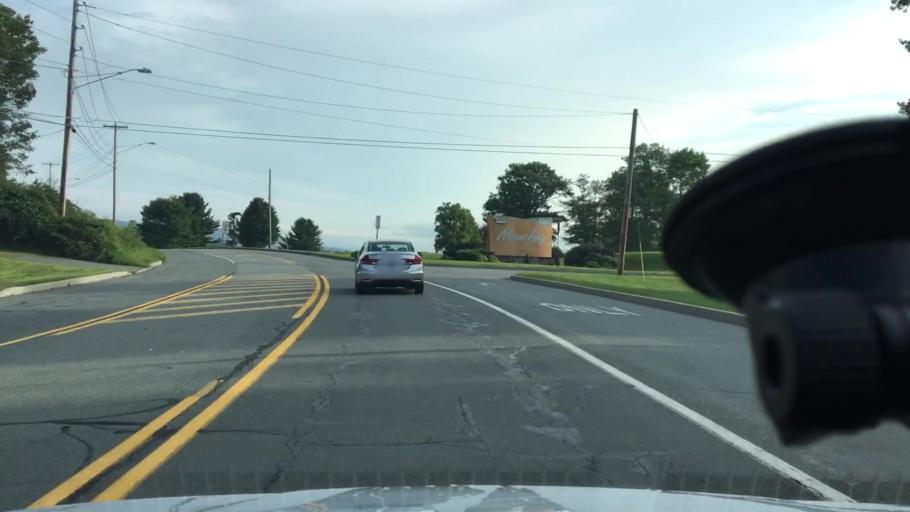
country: US
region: Pennsylvania
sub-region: Monroe County
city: Mount Pocono
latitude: 41.1059
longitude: -75.3268
